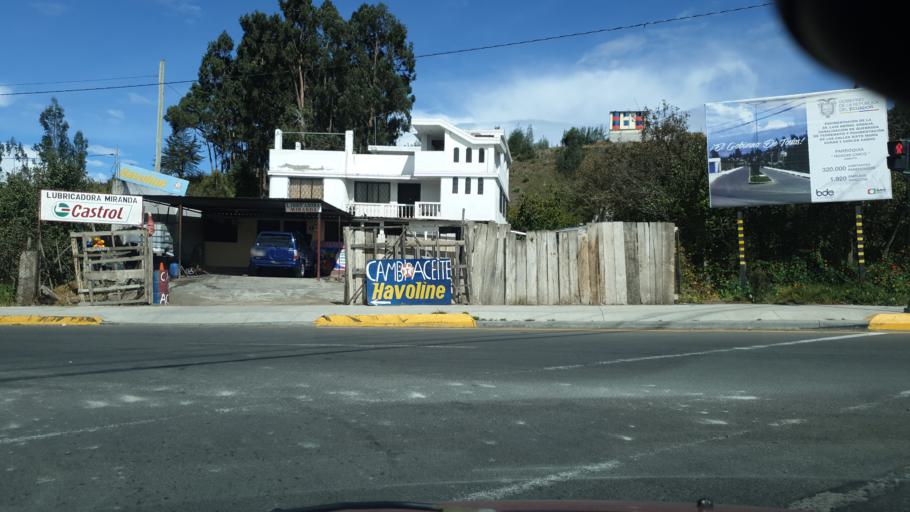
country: EC
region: Tungurahua
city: Ambato
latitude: -1.2964
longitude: -78.6354
